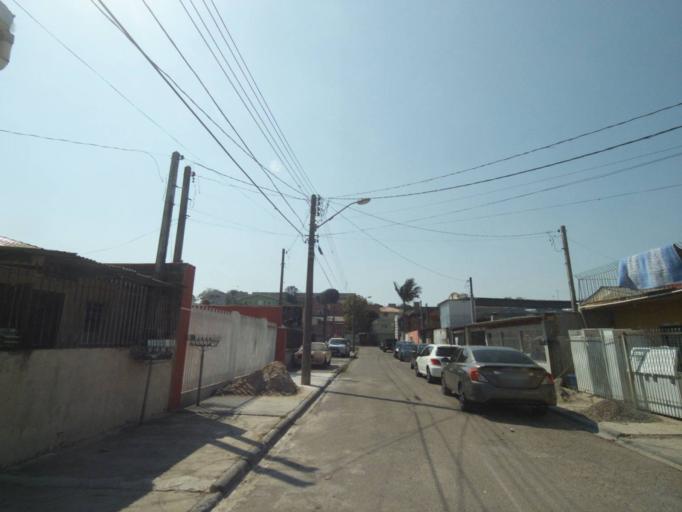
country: BR
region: Parana
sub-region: Curitiba
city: Curitiba
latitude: -25.4850
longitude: -49.3089
